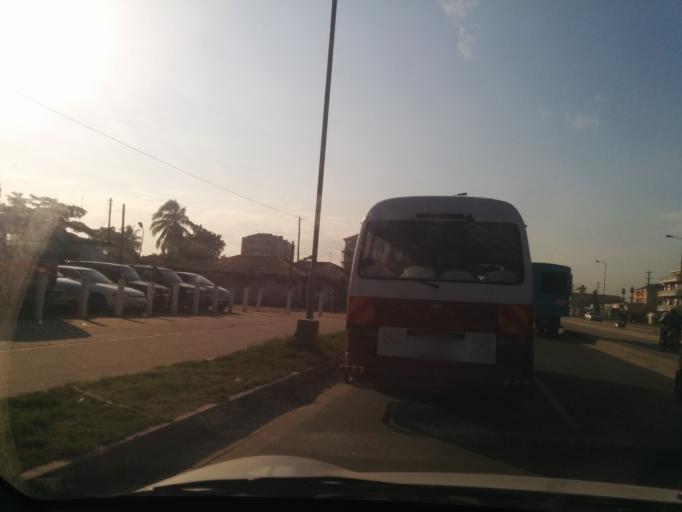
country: TZ
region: Dar es Salaam
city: Magomeni
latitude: -6.8032
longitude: 39.2465
